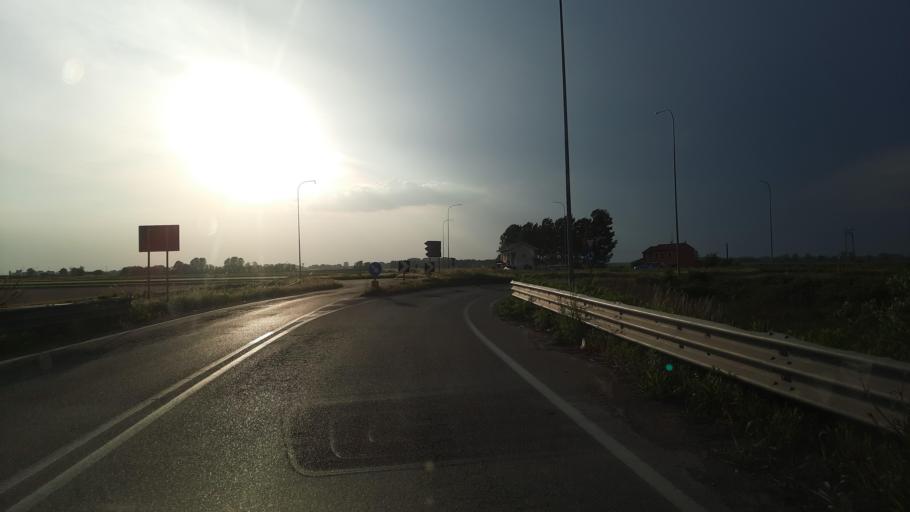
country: IT
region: Lombardy
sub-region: Provincia di Pavia
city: Cergnago
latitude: 45.2395
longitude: 8.7852
